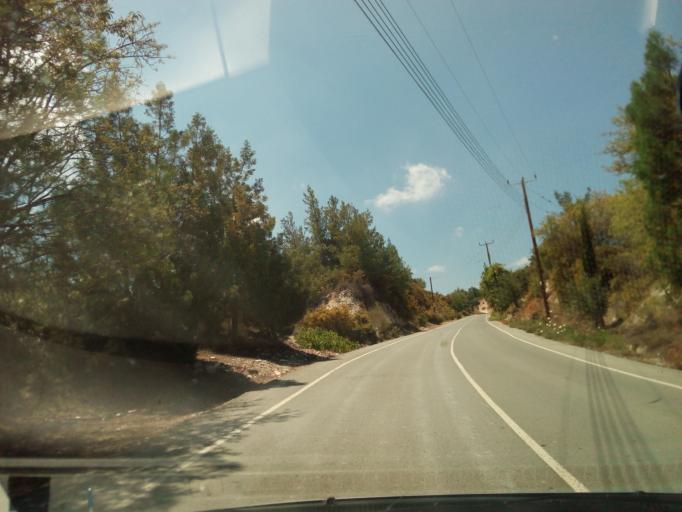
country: CY
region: Pafos
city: Mesogi
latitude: 34.9291
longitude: 32.6237
